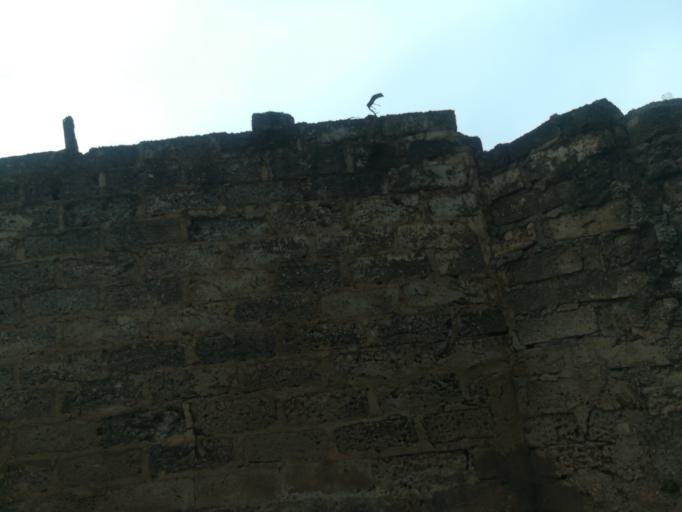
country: NG
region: Oyo
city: Ibadan
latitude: 7.3827
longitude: 3.9343
